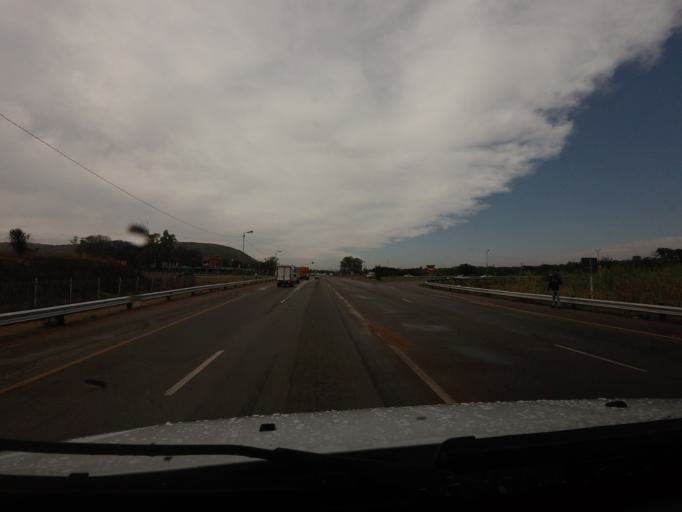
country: ZA
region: Gauteng
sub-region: City of Tshwane Metropolitan Municipality
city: Pretoria
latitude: -25.6847
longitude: 28.2920
